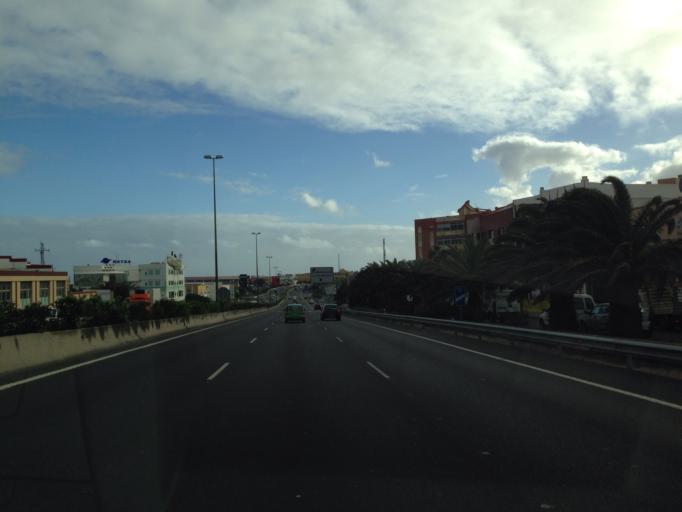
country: ES
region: Canary Islands
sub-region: Provincia de Las Palmas
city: Telde
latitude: 27.9838
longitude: -15.3921
